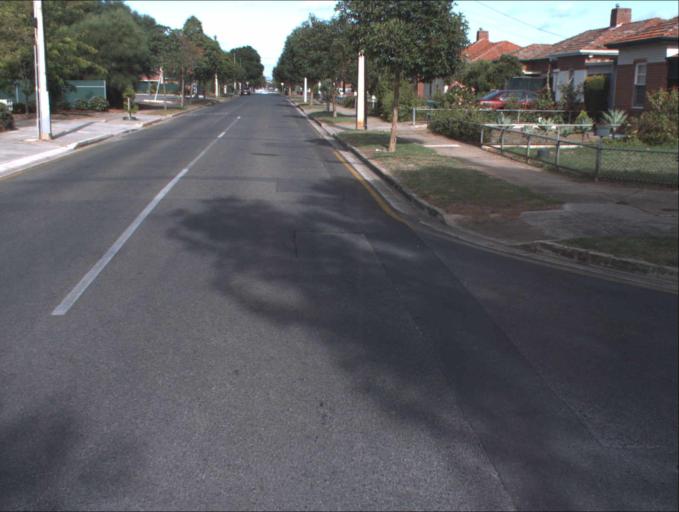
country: AU
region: South Australia
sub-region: Charles Sturt
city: Woodville North
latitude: -34.8655
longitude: 138.5537
